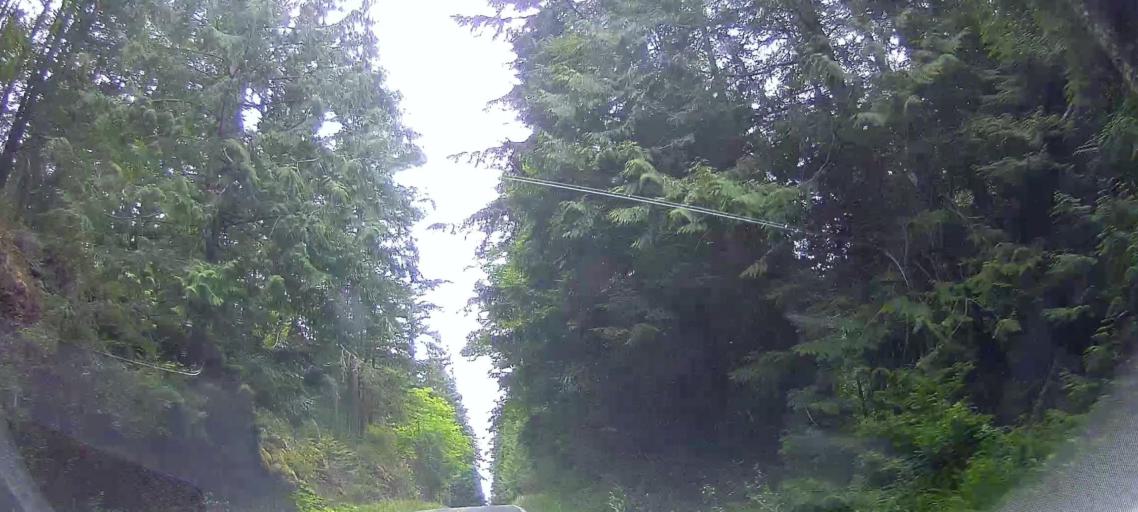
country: US
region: Washington
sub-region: Skagit County
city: Anacortes
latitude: 48.4635
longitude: -122.6336
